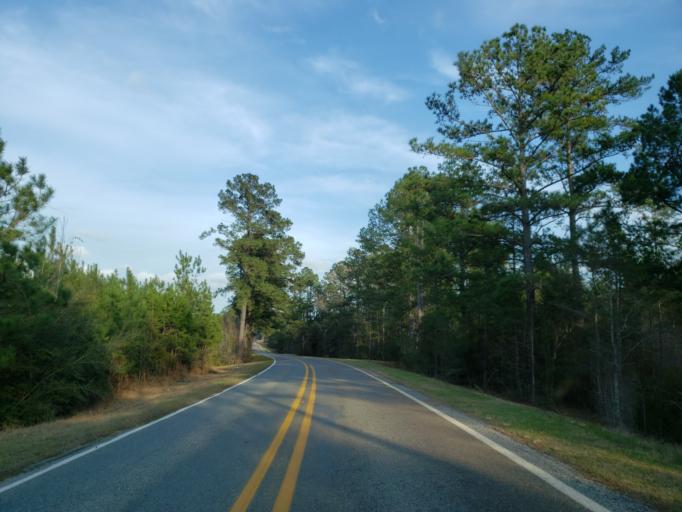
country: US
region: Mississippi
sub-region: Clarke County
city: Stonewall
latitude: 32.1744
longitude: -88.7874
